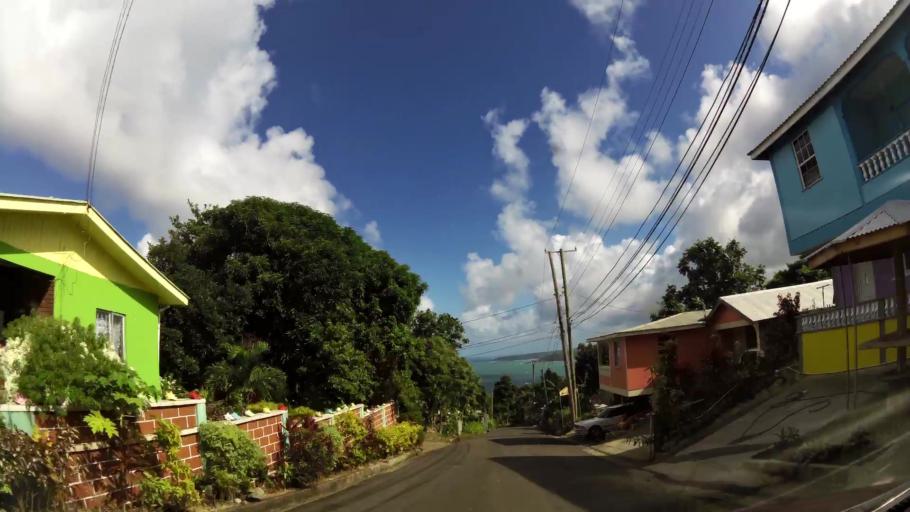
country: DM
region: Saint John
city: Portsmouth
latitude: 15.6182
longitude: -61.4091
